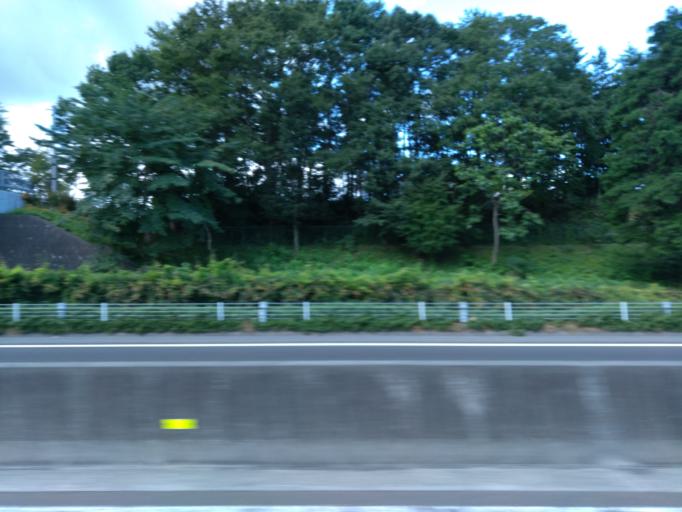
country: JP
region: Miyagi
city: Tomiya
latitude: 38.3350
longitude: 140.8555
